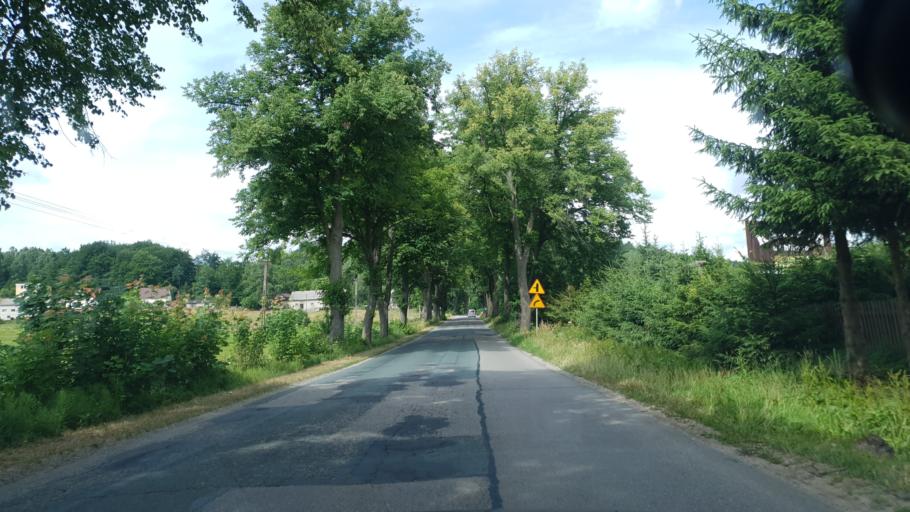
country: PL
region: Pomeranian Voivodeship
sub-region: Powiat kartuski
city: Chmielno
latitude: 54.2824
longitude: 18.1024
